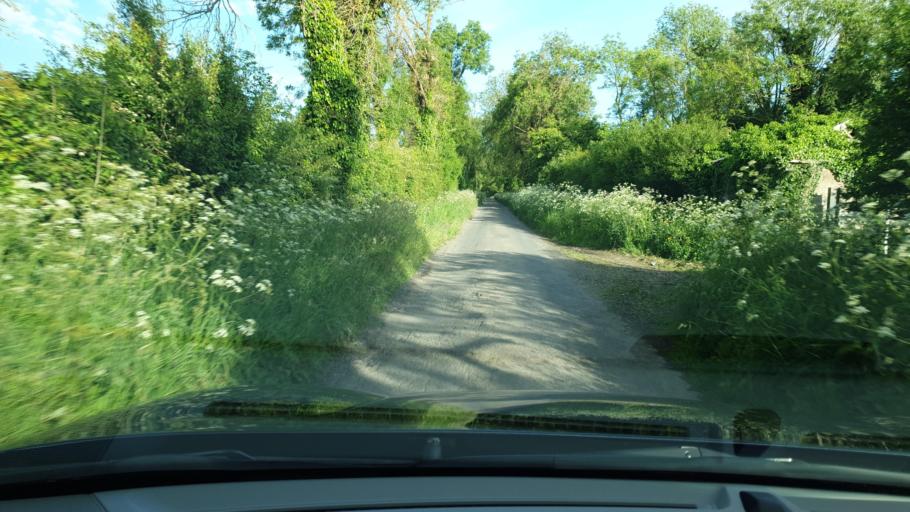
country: IE
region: Leinster
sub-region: An Mhi
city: Ashbourne
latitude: 53.5545
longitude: -6.4274
